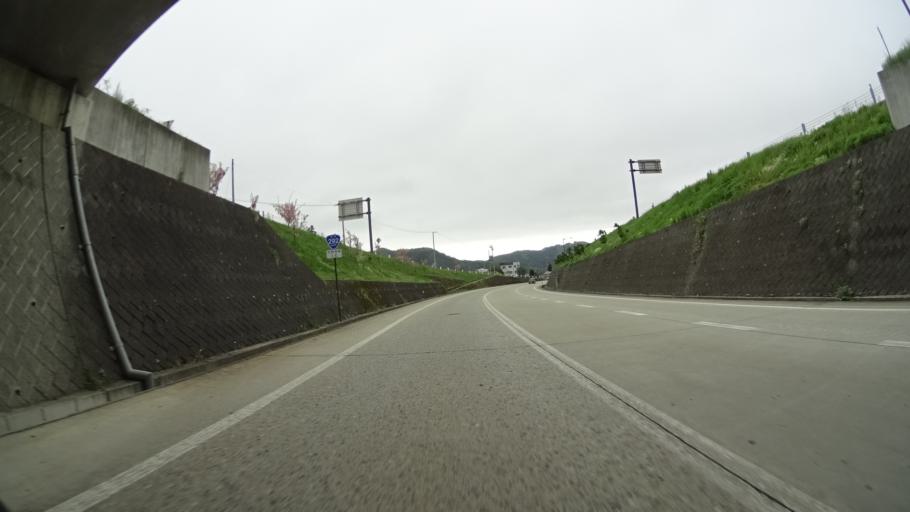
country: JP
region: Nagano
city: Nakano
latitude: 36.7346
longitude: 138.4154
